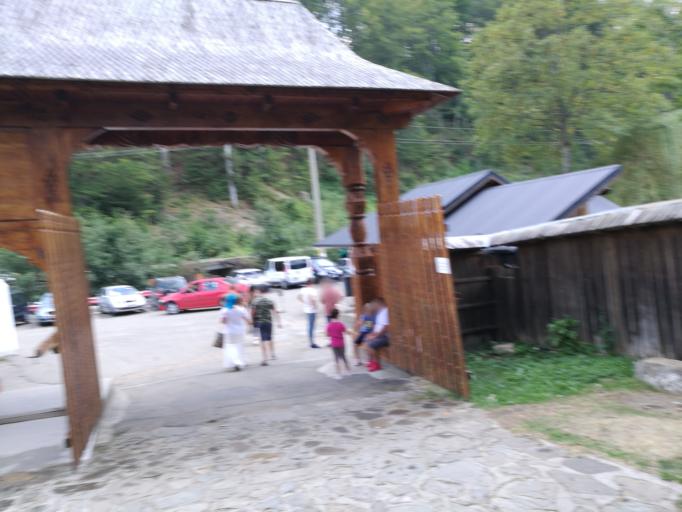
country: RO
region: Neamt
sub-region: Comuna Pipirig
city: Stanca
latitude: 47.1751
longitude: 26.1686
